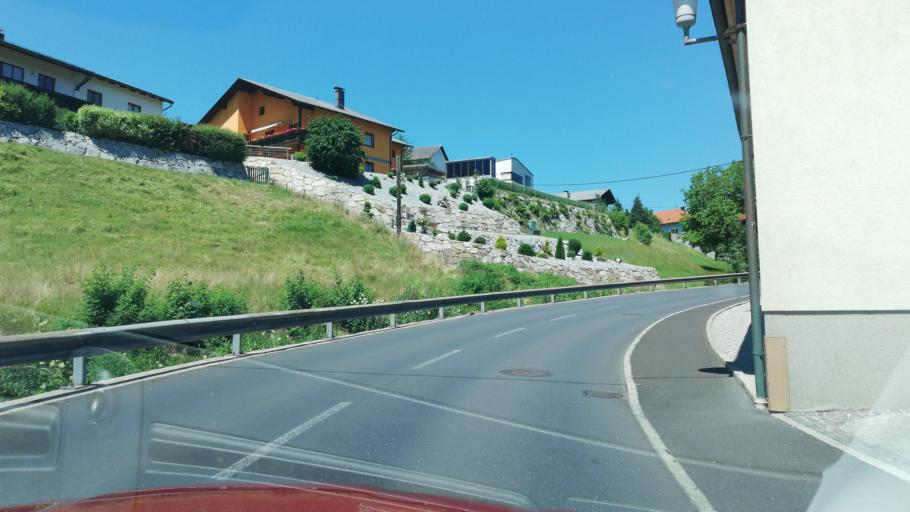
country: AT
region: Upper Austria
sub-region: Politischer Bezirk Urfahr-Umgebung
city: Reichenau im Muhlkreis
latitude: 48.4531
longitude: 14.3520
